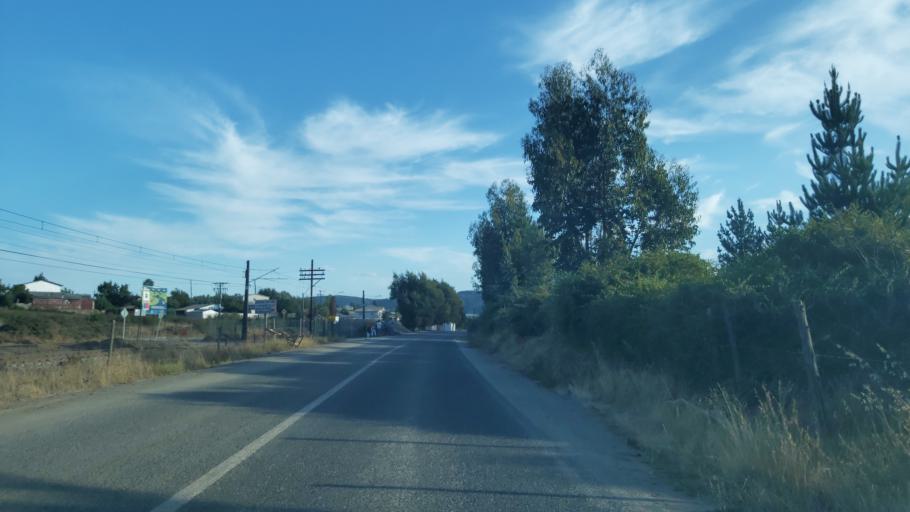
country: CL
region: Biobio
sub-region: Provincia de Biobio
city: La Laja
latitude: -37.1546
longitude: -72.9171
